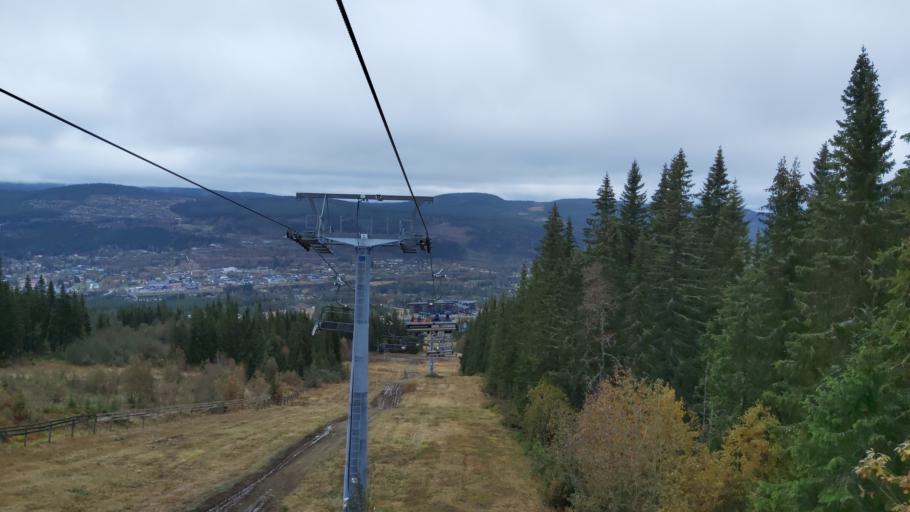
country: NO
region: Hedmark
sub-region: Trysil
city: Innbygda
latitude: 61.3082
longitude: 12.2217
